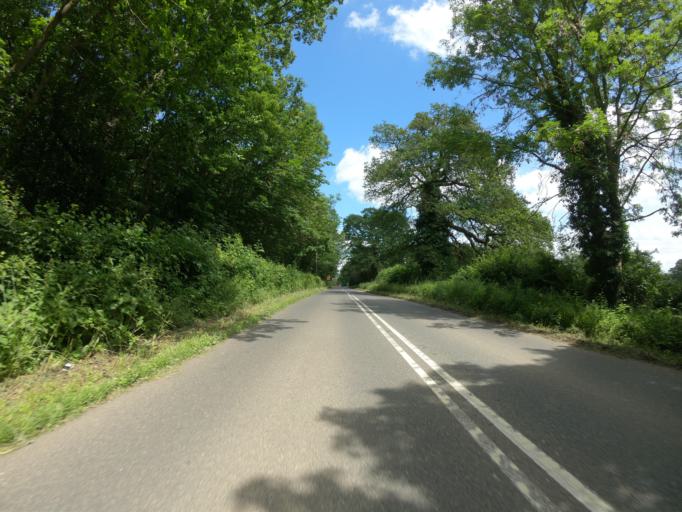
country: GB
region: England
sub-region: Kent
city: Halstead
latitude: 51.2919
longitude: 0.1374
